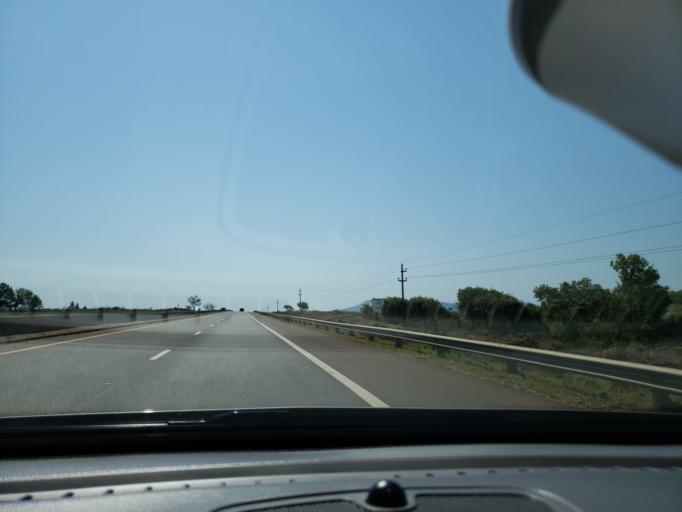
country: AR
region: Misiones
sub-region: Departamento de Candelaria
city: Candelaria
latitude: -27.4572
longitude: -55.6675
